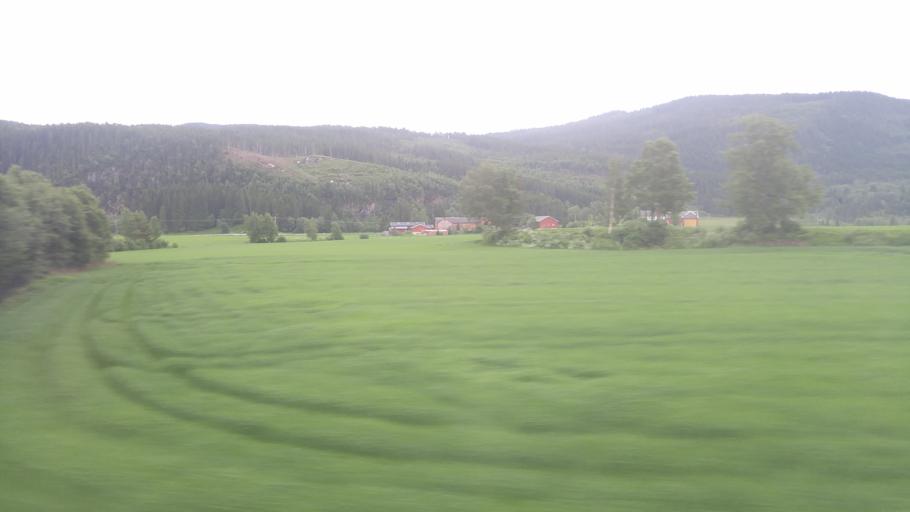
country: NO
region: Nord-Trondelag
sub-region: Stjordal
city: Stjordalshalsen
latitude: 63.4591
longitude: 11.0837
